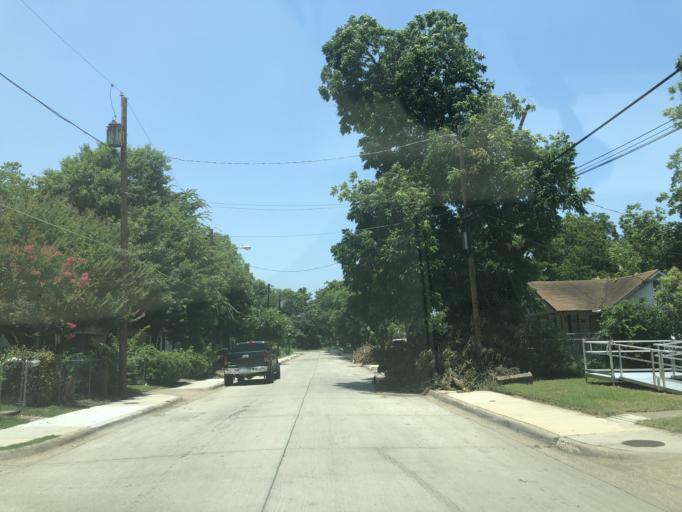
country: US
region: Texas
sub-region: Dallas County
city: Dallas
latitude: 32.7847
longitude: -96.8422
